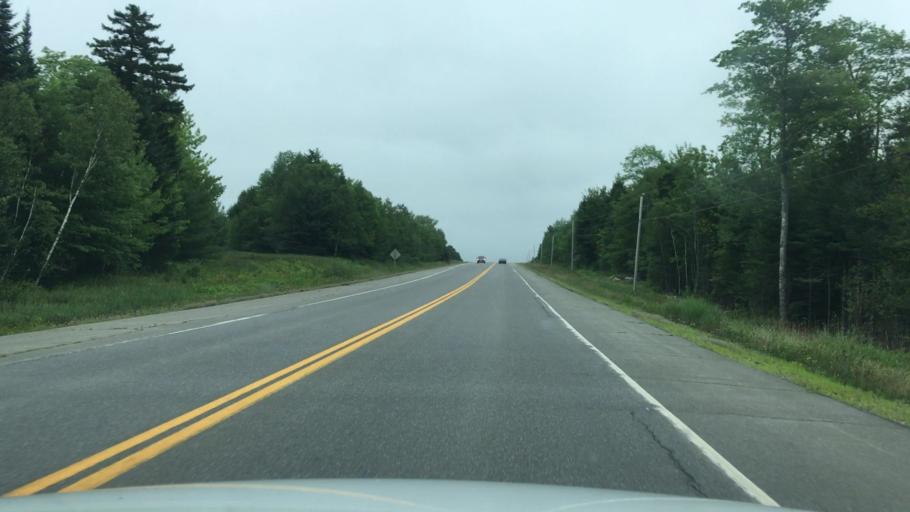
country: US
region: Maine
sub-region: Hancock County
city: Franklin
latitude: 44.8291
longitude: -68.1279
